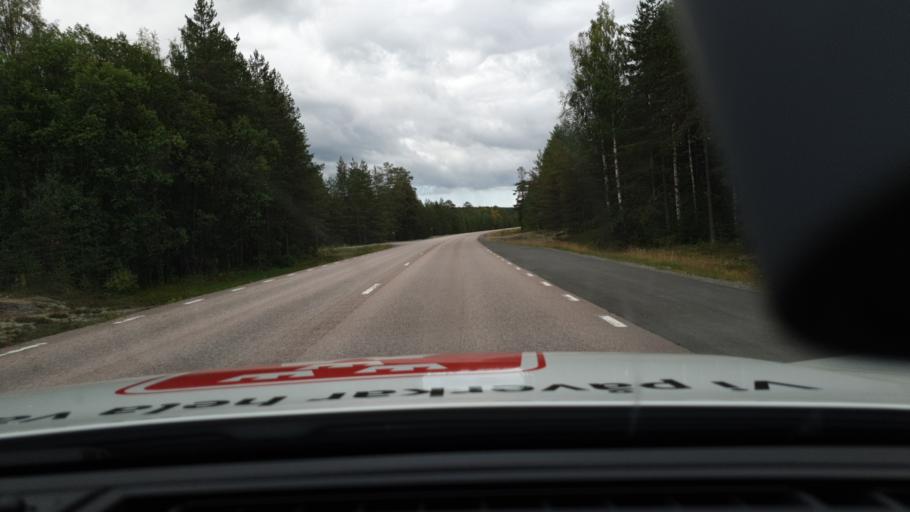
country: SE
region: Norrbotten
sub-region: Kalix Kommun
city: Toere
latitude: 66.0484
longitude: 22.7179
